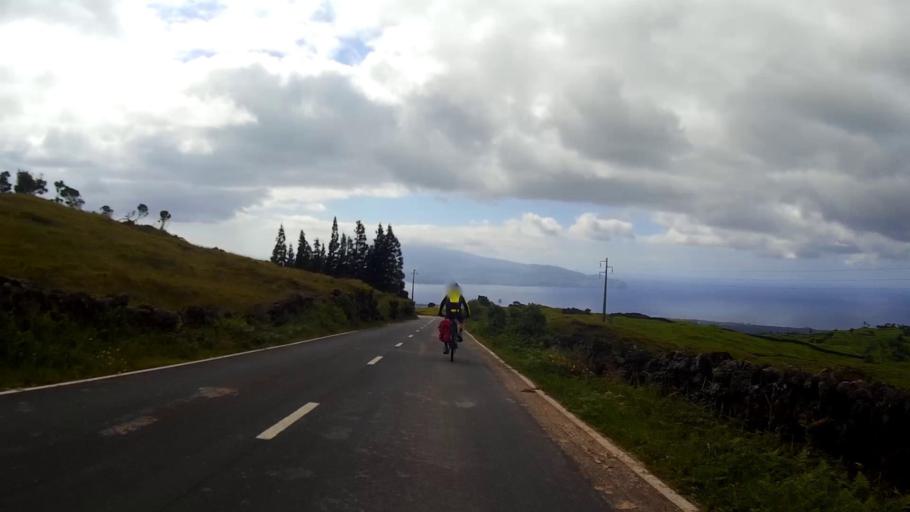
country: PT
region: Azores
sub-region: Madalena
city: Madalena
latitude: 38.4967
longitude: -28.4487
